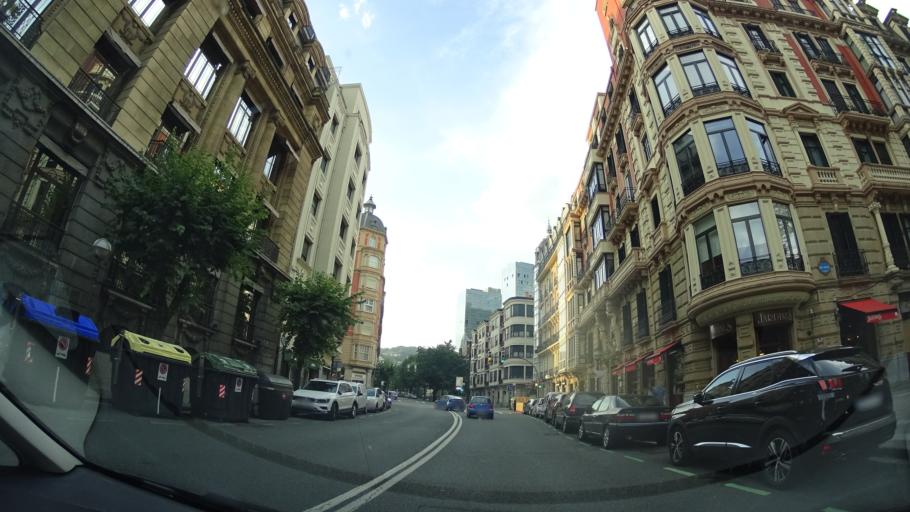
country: ES
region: Basque Country
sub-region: Bizkaia
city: Bilbao
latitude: 43.2638
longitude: -2.9290
